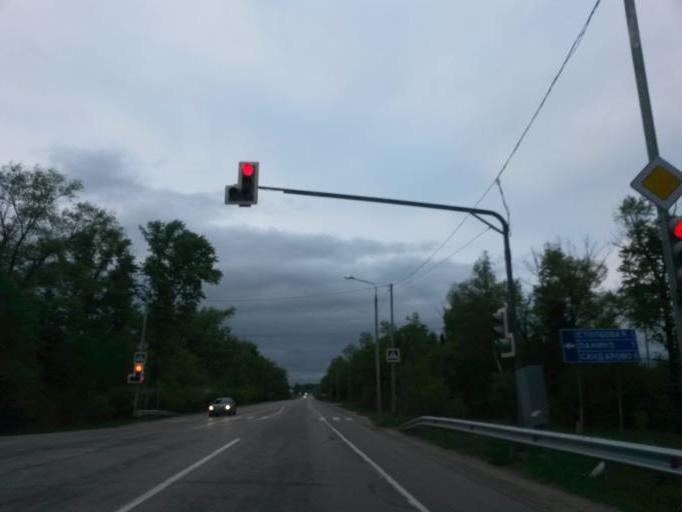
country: RU
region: Moskovskaya
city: Stolbovaya
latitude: 55.2571
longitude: 37.5086
